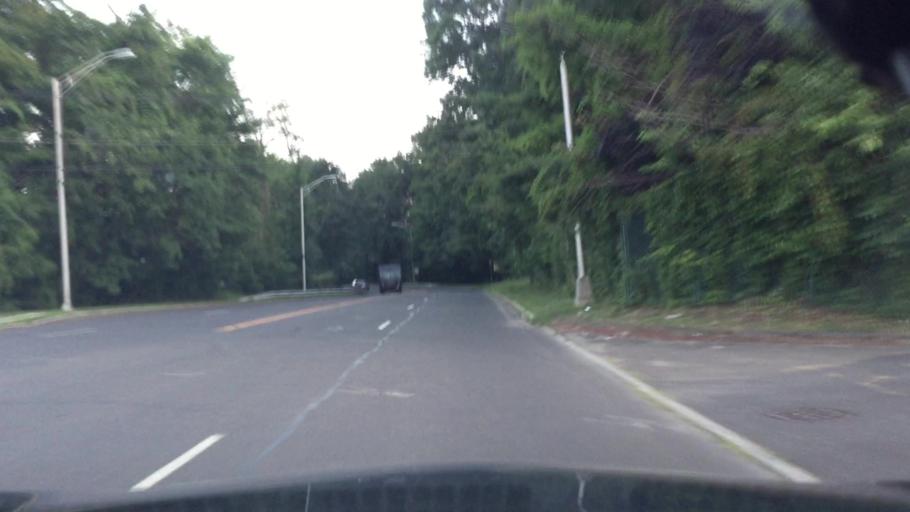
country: US
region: Connecticut
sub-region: Fairfield County
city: Darien
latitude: 41.0780
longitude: -73.4285
